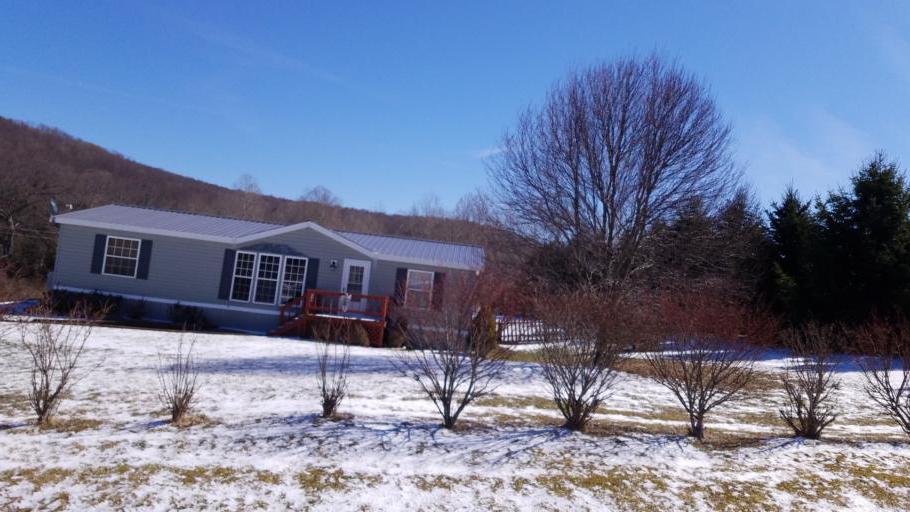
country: US
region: New York
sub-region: Allegany County
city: Andover
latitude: 42.0357
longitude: -77.7609
